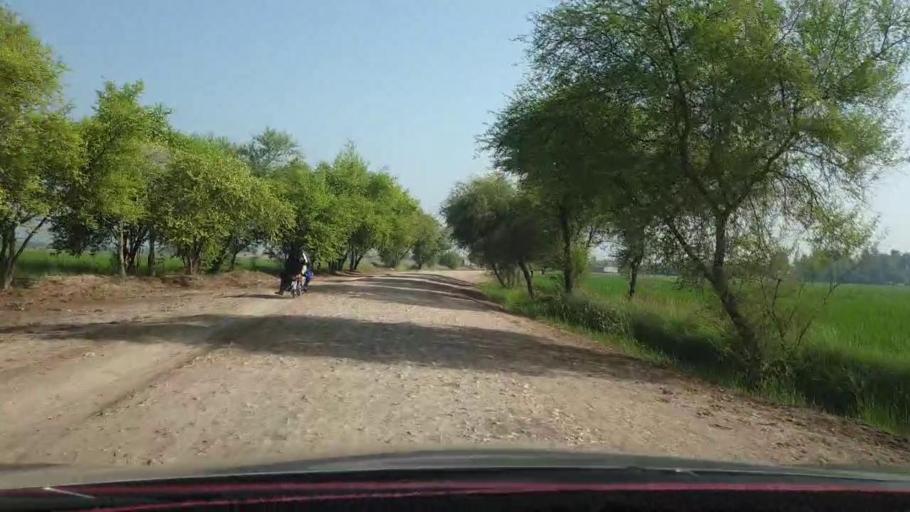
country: PK
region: Sindh
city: Nasirabad
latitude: 27.4583
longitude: 67.9179
